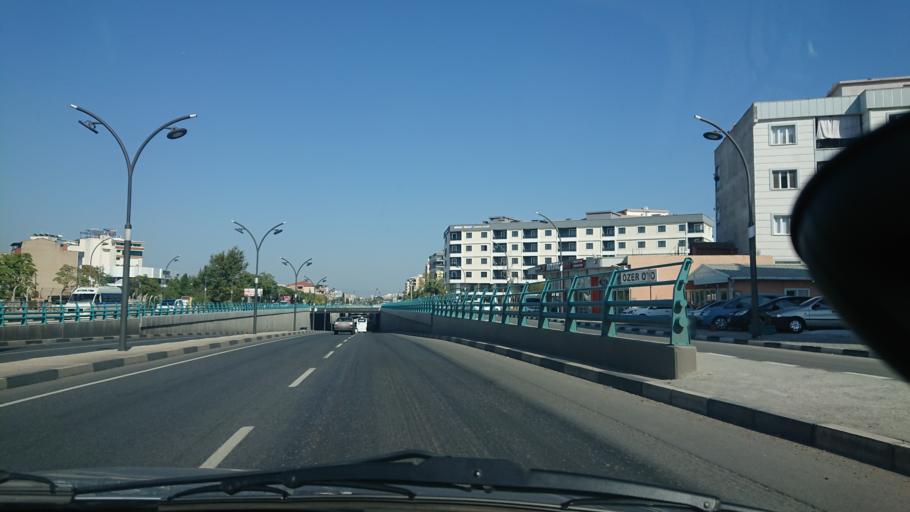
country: TR
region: Manisa
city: Turgutlu
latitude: 38.4891
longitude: 27.6991
